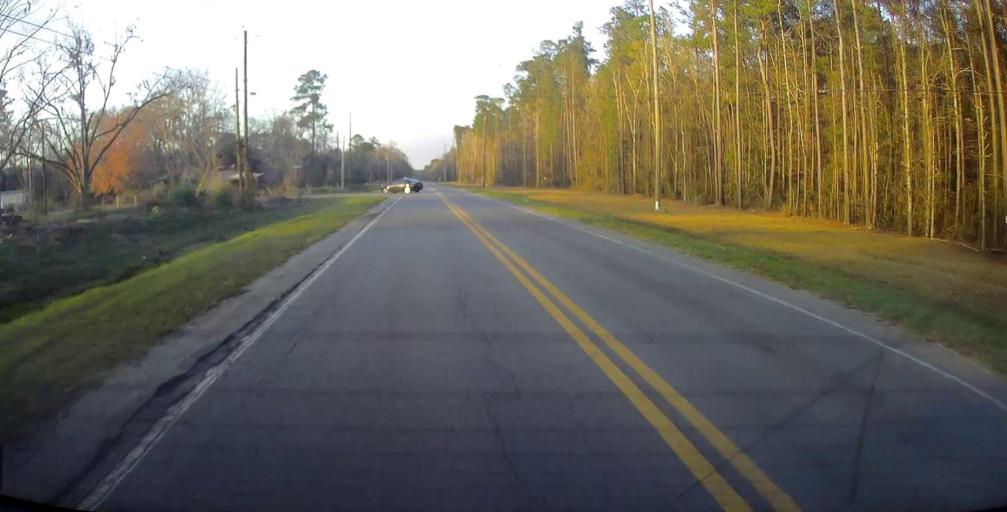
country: US
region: Georgia
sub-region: Chatham County
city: Bloomingdale
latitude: 32.1490
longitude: -81.3893
